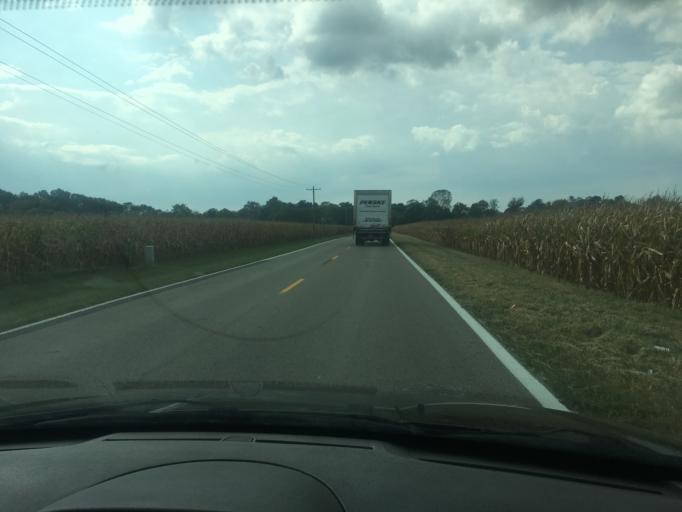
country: US
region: Ohio
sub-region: Champaign County
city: Urbana
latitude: 40.1562
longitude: -83.8154
